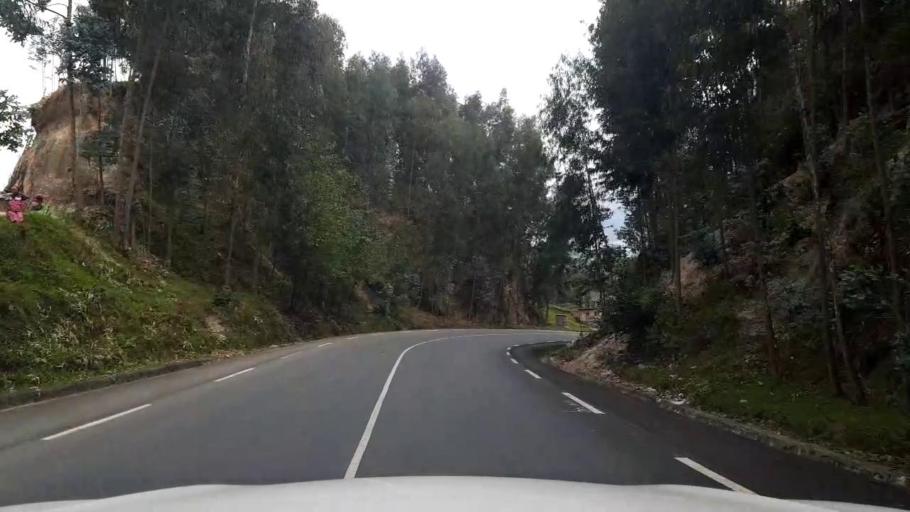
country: RW
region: Northern Province
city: Musanze
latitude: -1.6759
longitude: 29.5172
